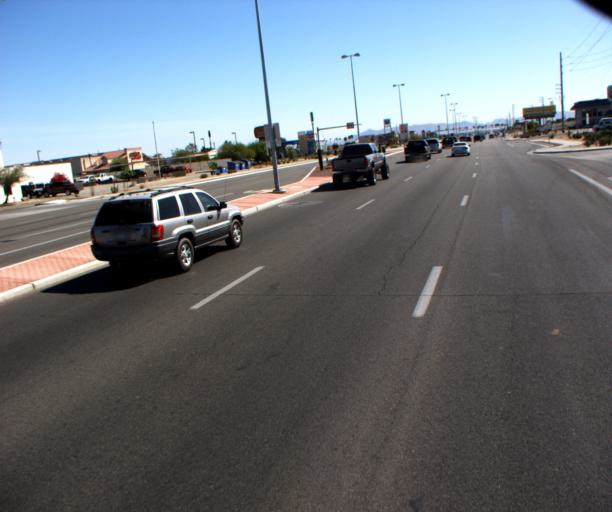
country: US
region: Arizona
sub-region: Yuma County
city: Yuma
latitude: 32.6984
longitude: -114.6154
